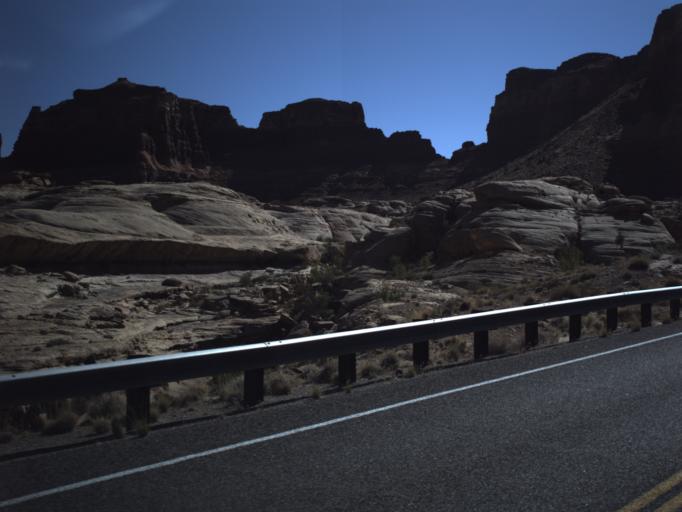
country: US
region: Utah
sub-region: San Juan County
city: Blanding
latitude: 37.9037
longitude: -110.3793
